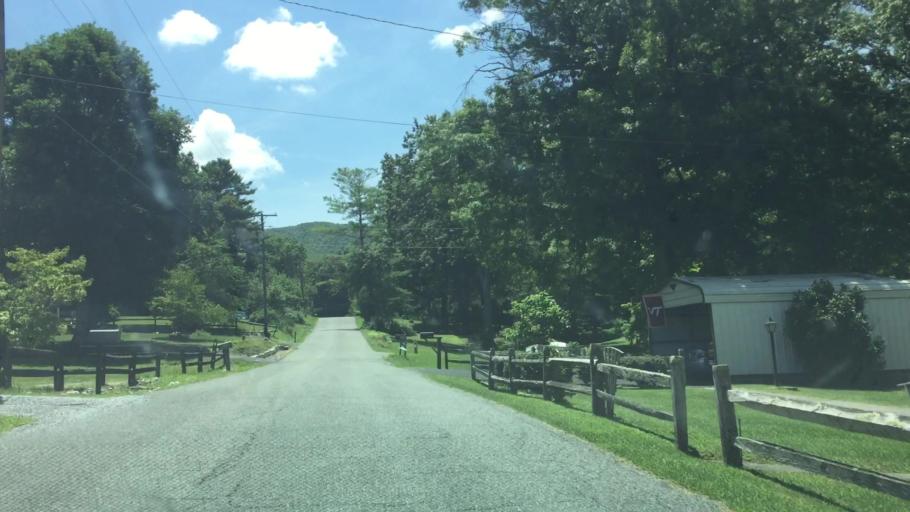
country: US
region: Virginia
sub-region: Wythe County
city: Wytheville
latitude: 36.9354
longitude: -81.0010
